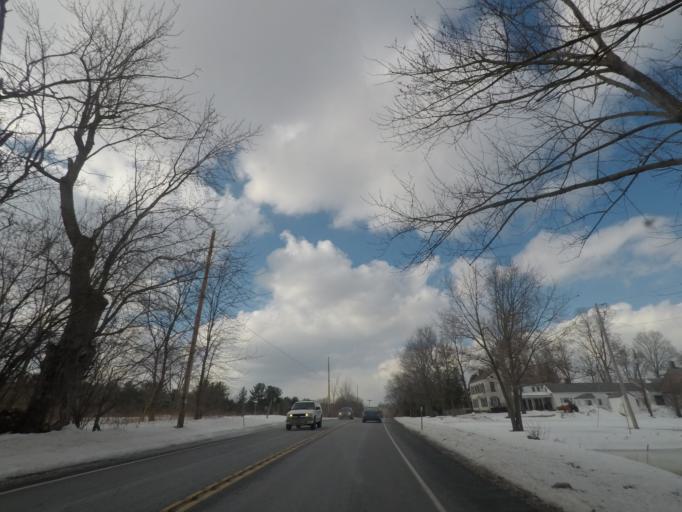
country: US
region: New York
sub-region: Saratoga County
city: Country Knolls
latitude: 42.8682
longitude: -73.8585
